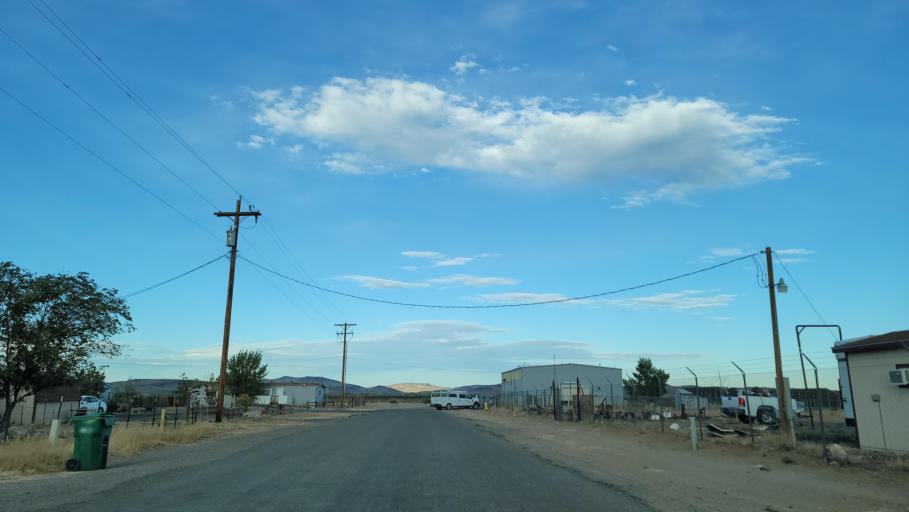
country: US
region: Nevada
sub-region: Lyon County
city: Silver Springs
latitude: 39.4044
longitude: -119.2158
